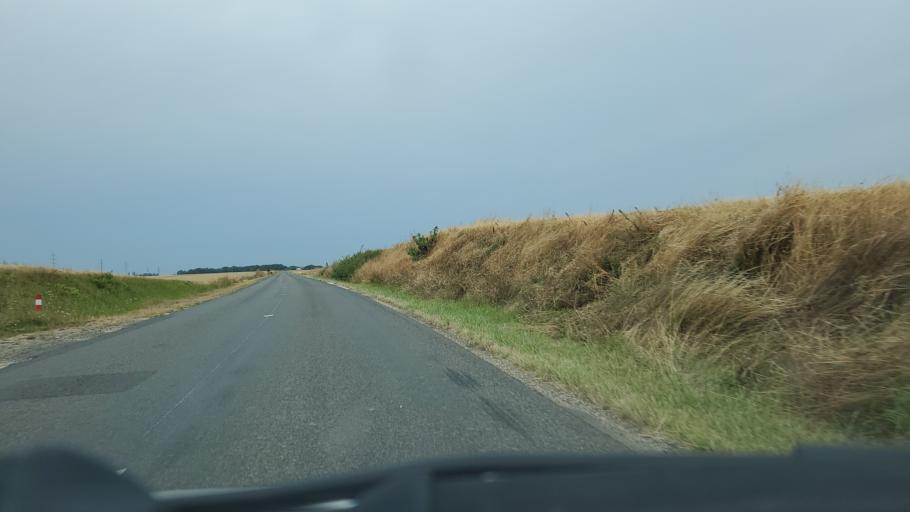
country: FR
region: Ile-de-France
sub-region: Departement de Seine-et-Marne
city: Chailly-en-Brie
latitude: 48.7840
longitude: 3.1513
